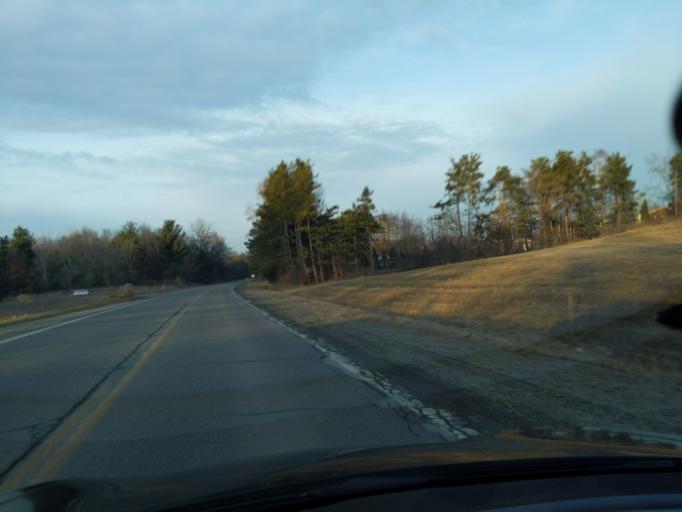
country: US
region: Michigan
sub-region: Livingston County
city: Brighton
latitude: 42.5948
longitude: -83.7536
